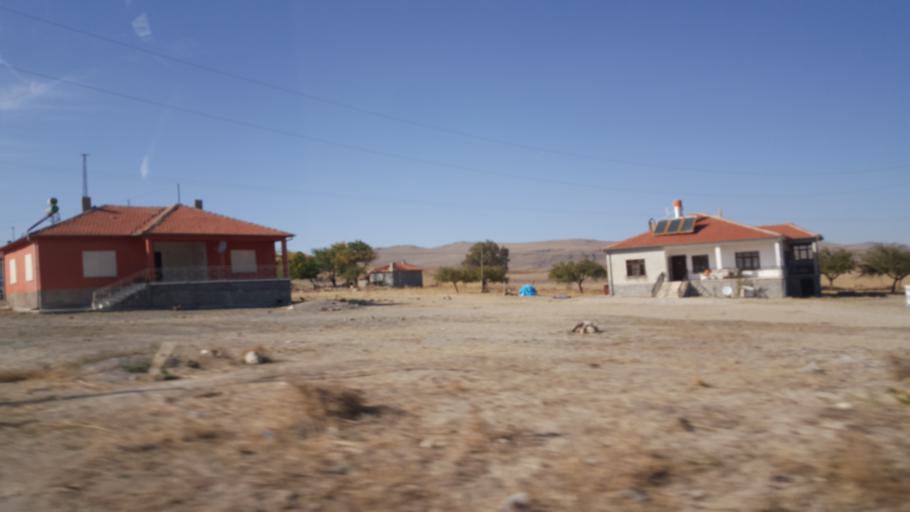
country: TR
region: Ankara
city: Altpinar
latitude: 39.2453
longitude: 32.7473
